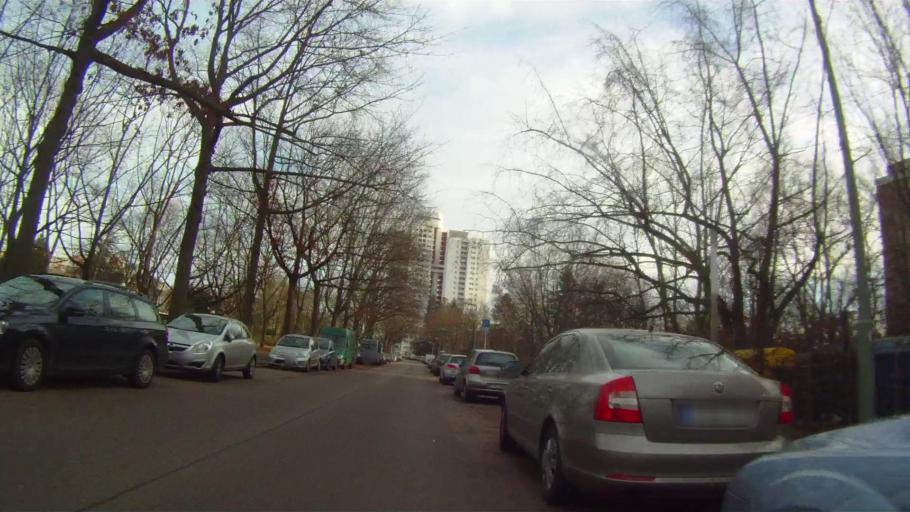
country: DE
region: Berlin
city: Gropiusstadt
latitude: 52.4233
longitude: 13.4694
